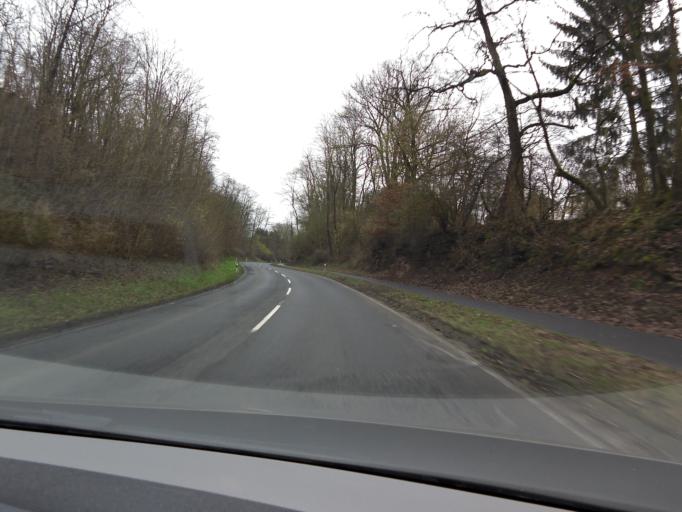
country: DE
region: Hesse
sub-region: Regierungsbezirk Kassel
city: Eschwege
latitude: 51.1797
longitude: 10.0734
